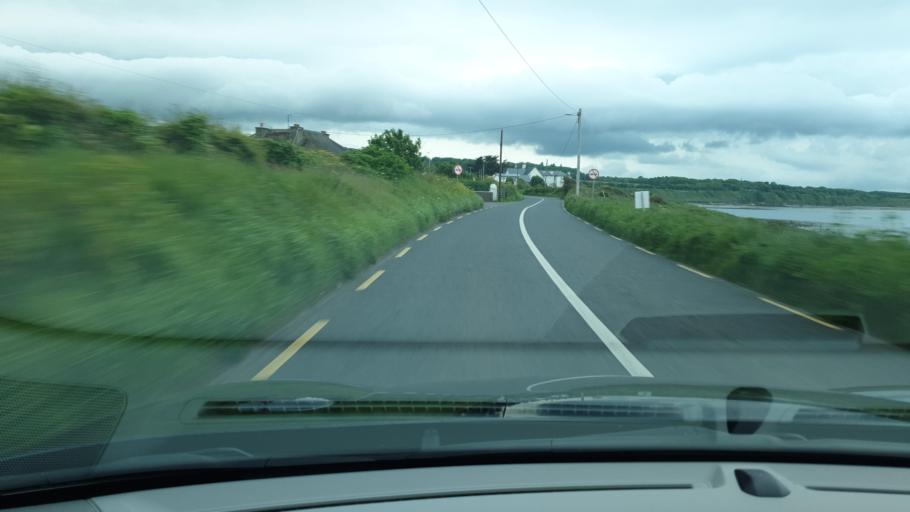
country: IE
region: Leinster
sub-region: Fingal County
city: Skerries
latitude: 53.5863
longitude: -6.1374
